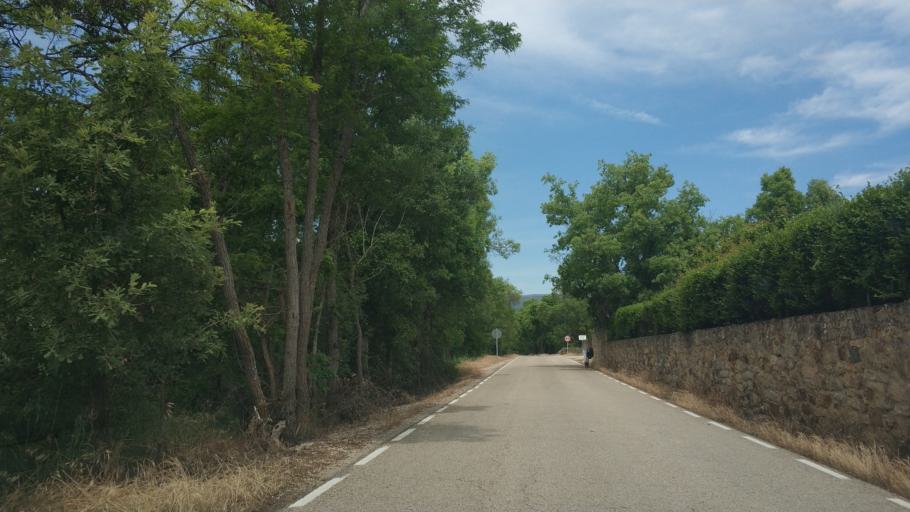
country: ES
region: Castille and Leon
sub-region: Provincia de Soria
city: Sotillo del Rincon
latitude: 41.9010
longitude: -2.6400
